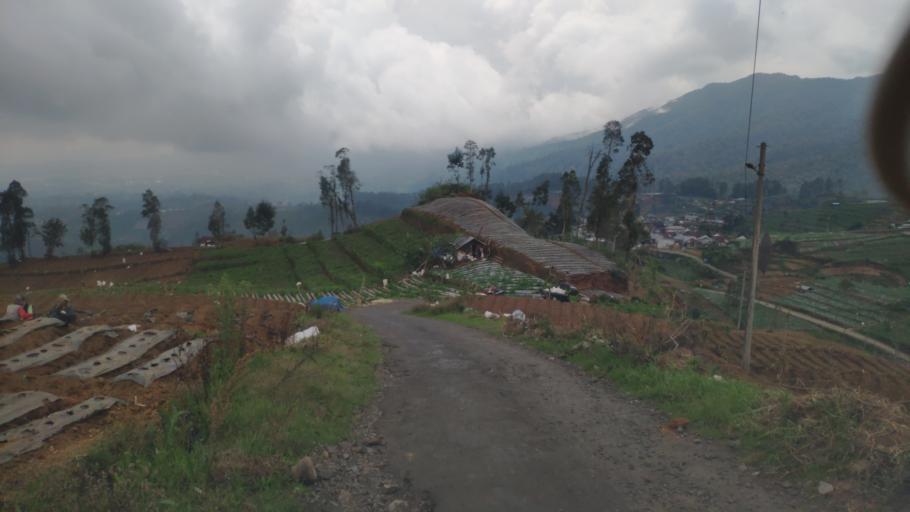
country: ID
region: Central Java
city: Wonosobo
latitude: -7.1922
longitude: 109.8105
